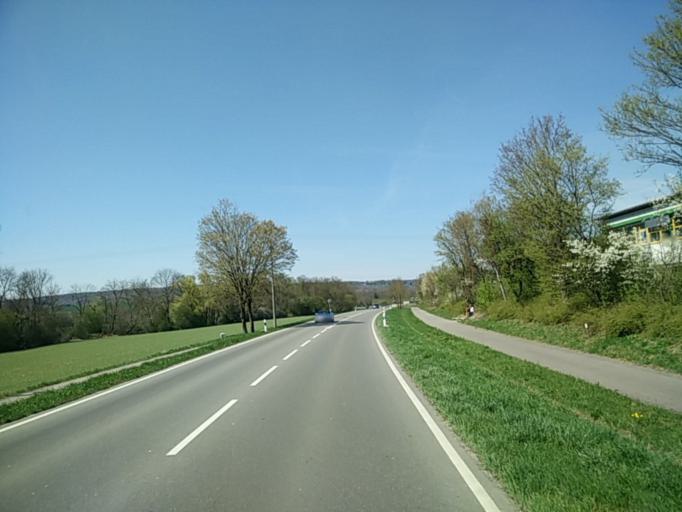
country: DE
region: Baden-Wuerttemberg
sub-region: Tuebingen Region
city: Gomaringen
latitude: 48.4567
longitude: 9.0788
